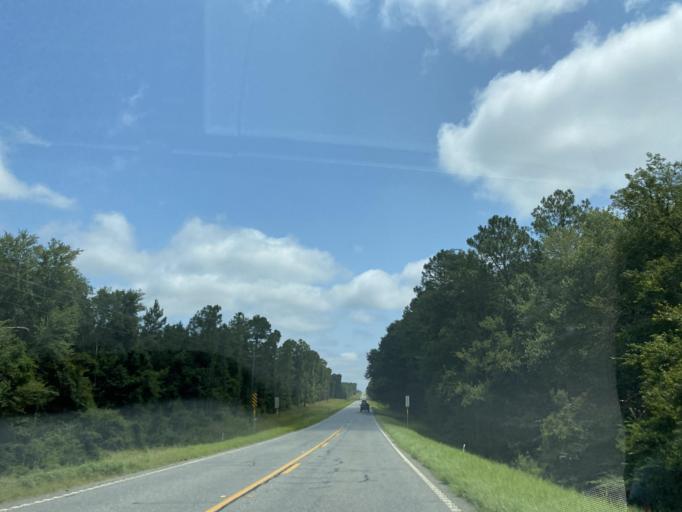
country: US
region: Georgia
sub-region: Telfair County
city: McRae
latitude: 32.0994
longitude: -82.8449
